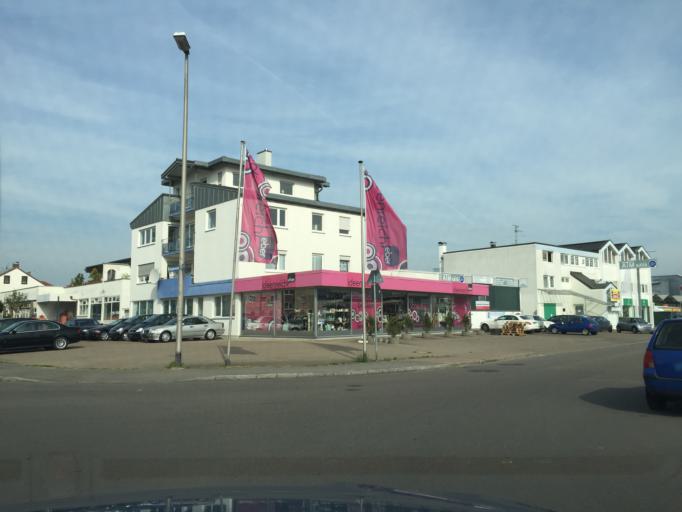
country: DE
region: Bavaria
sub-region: Swabia
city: Senden
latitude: 48.3285
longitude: 10.0433
